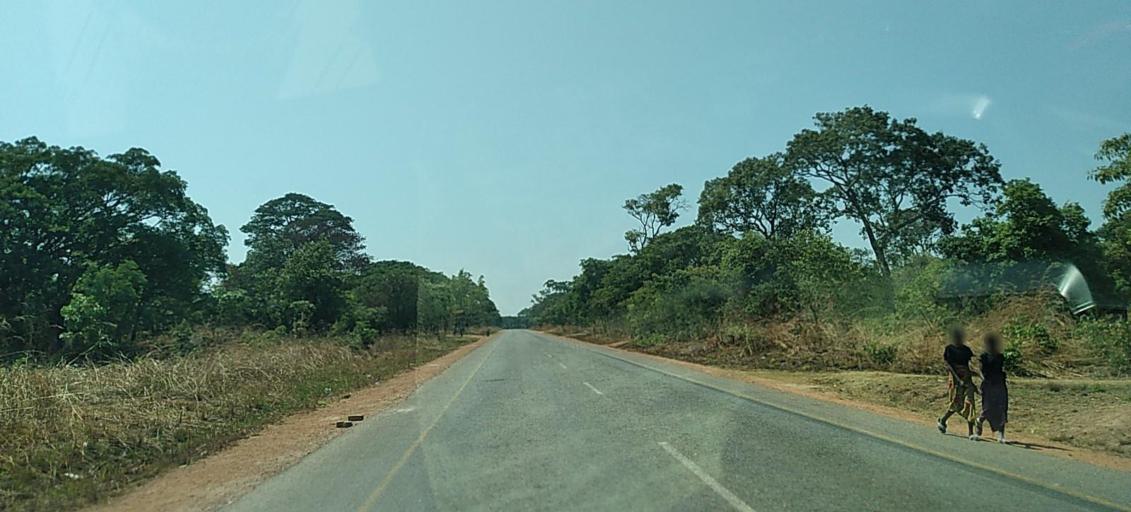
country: ZM
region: North-Western
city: Solwezi
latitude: -12.2931
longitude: 25.6987
